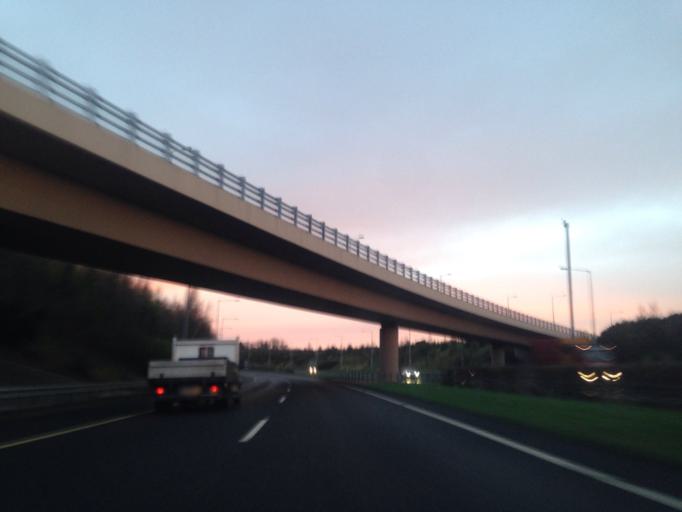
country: IE
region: Leinster
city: Shankill
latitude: 53.2314
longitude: -6.1324
